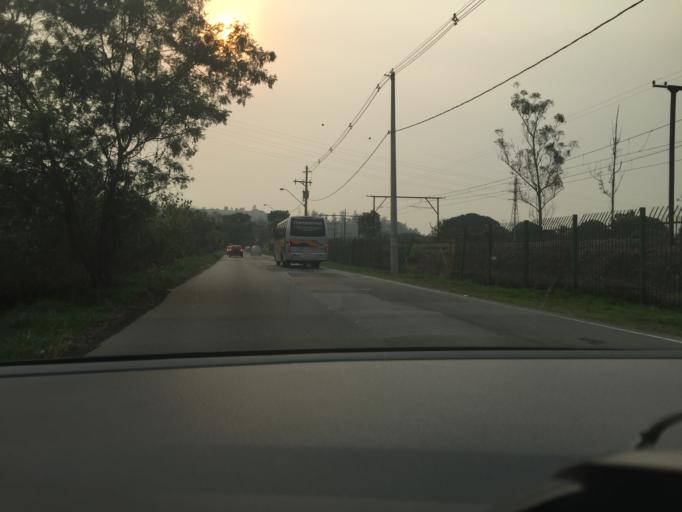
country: BR
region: Sao Paulo
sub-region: Varzea Paulista
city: Varzea Paulista
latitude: -23.2029
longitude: -46.8489
